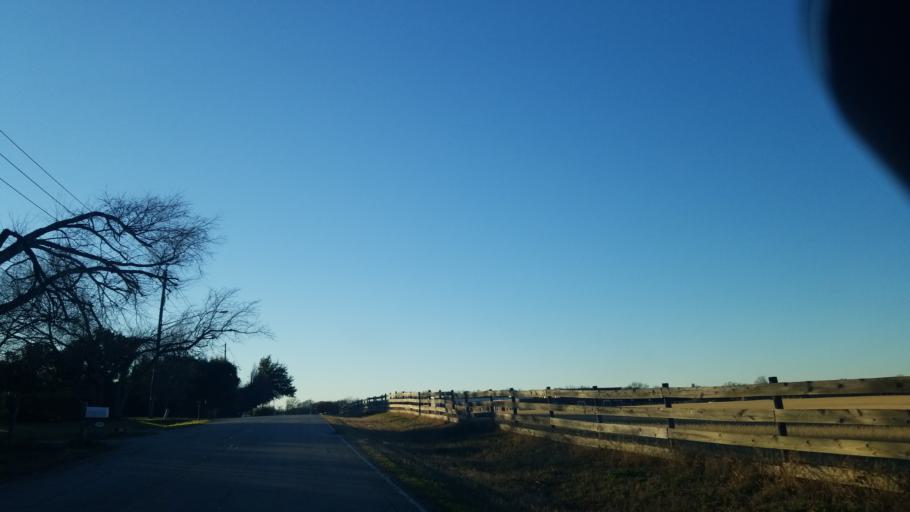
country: US
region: Texas
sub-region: Denton County
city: Shady Shores
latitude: 33.1445
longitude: -97.0324
